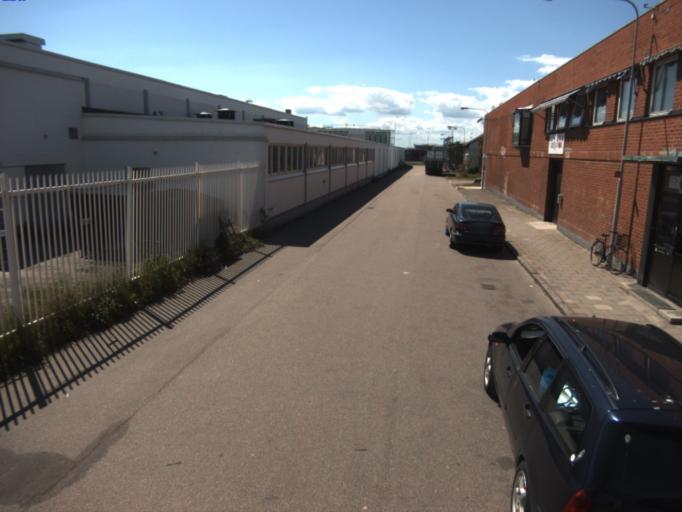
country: SE
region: Skane
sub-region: Helsingborg
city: Helsingborg
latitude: 56.0293
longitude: 12.7049
